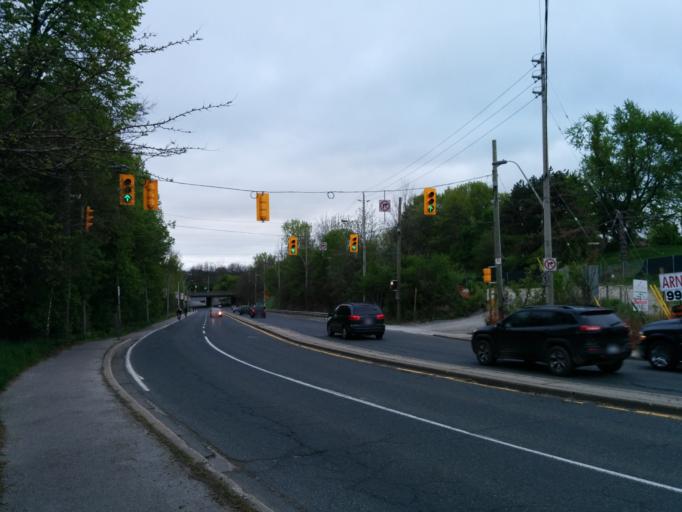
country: CA
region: Ontario
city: Toronto
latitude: 43.6963
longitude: -79.3697
